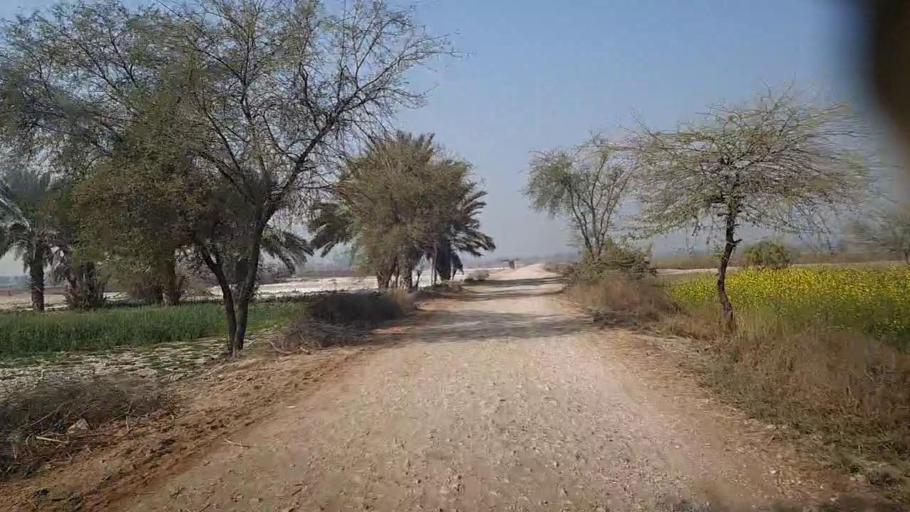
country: PK
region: Sindh
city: Karaundi
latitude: 26.8474
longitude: 68.3955
